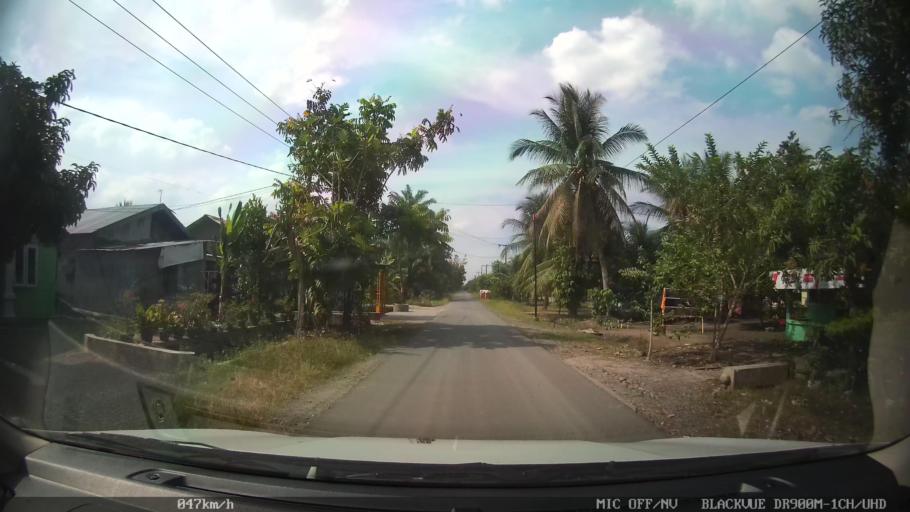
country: ID
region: North Sumatra
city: Binjai
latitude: 3.6447
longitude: 98.5174
